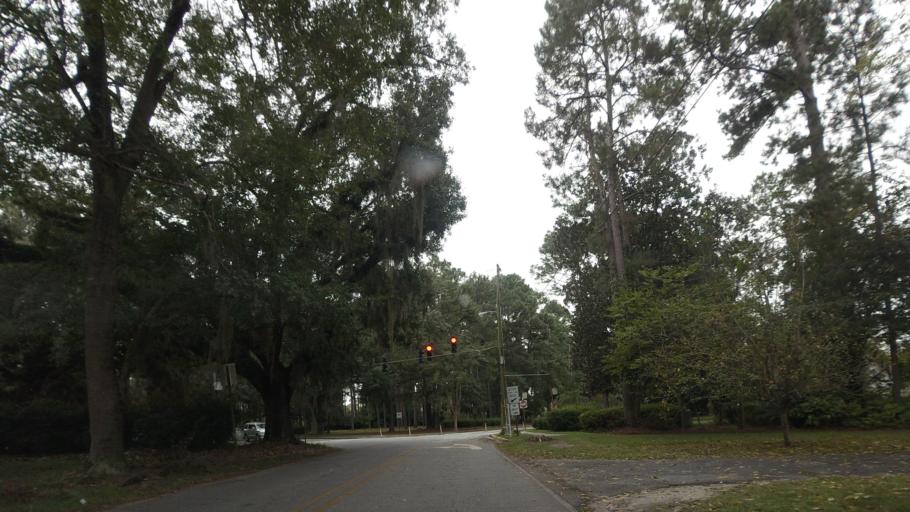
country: US
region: Georgia
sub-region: Lowndes County
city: Remerton
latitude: 30.8513
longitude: -83.2931
